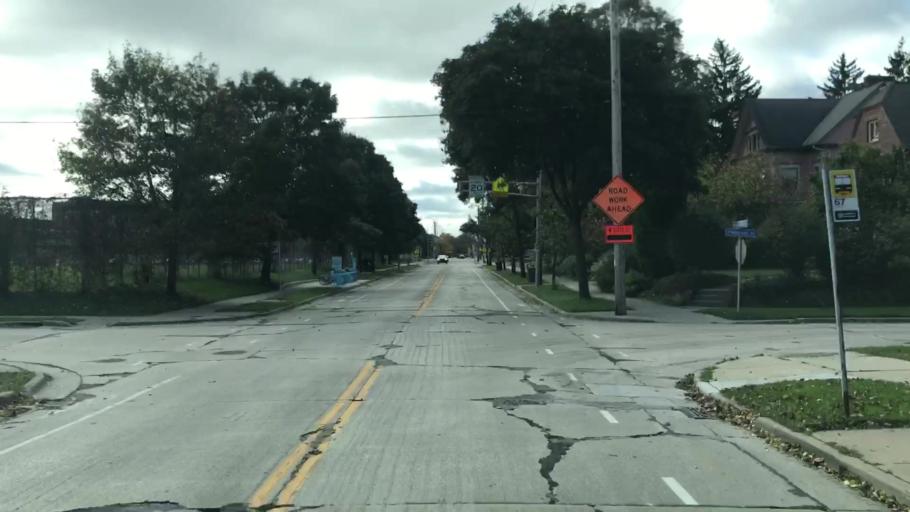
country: US
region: Wisconsin
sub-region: Milwaukee County
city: Wauwatosa
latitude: 43.0554
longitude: -88.0074
